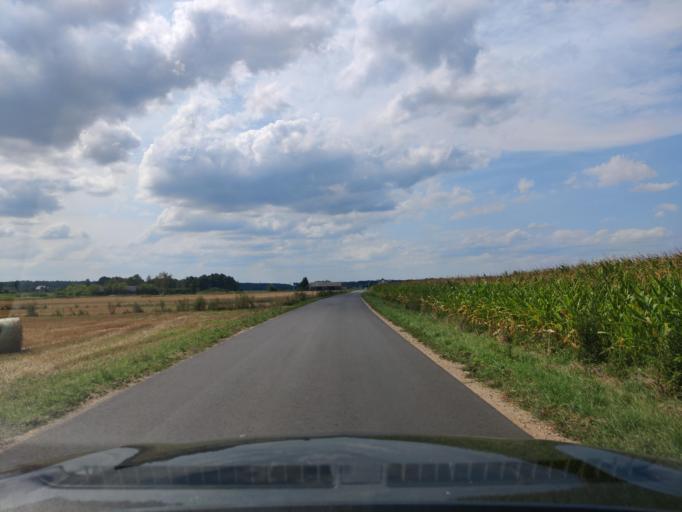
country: PL
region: Masovian Voivodeship
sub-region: Powiat pultuski
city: Obryte
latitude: 52.6920
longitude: 21.2036
